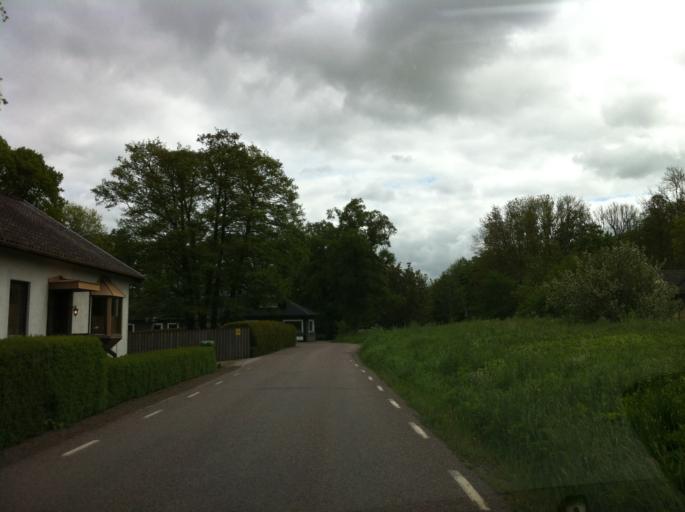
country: SE
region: Skane
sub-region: Kavlinge Kommun
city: Kaevlinge
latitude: 55.8146
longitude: 13.0607
